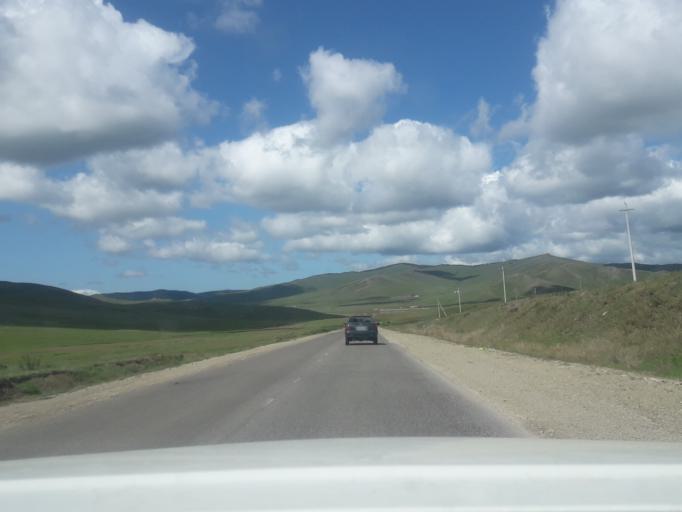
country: MN
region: Central Aimak
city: Ihsueuej
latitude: 48.1532
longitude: 106.4073
